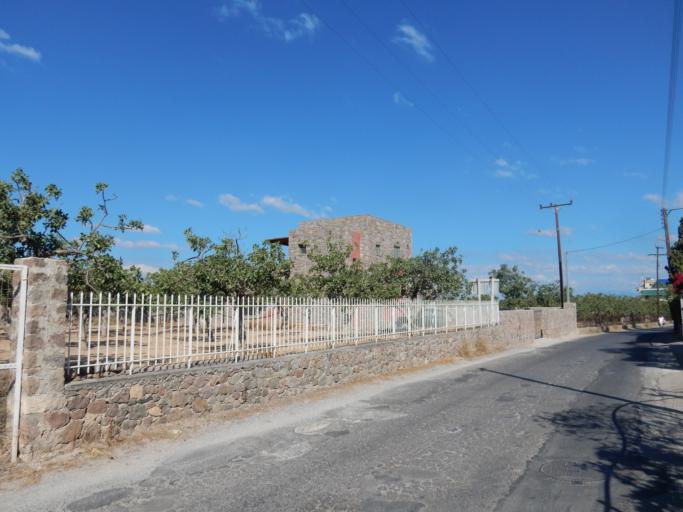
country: GR
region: Attica
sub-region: Nomos Piraios
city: Aegina
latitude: 37.7304
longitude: 23.4433
